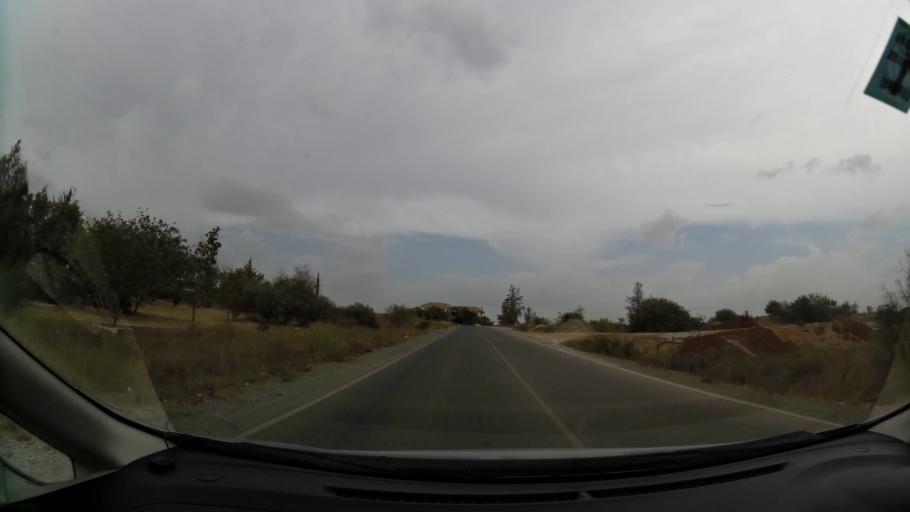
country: CY
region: Lefkosia
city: Geri
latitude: 35.0815
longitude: 33.3960
